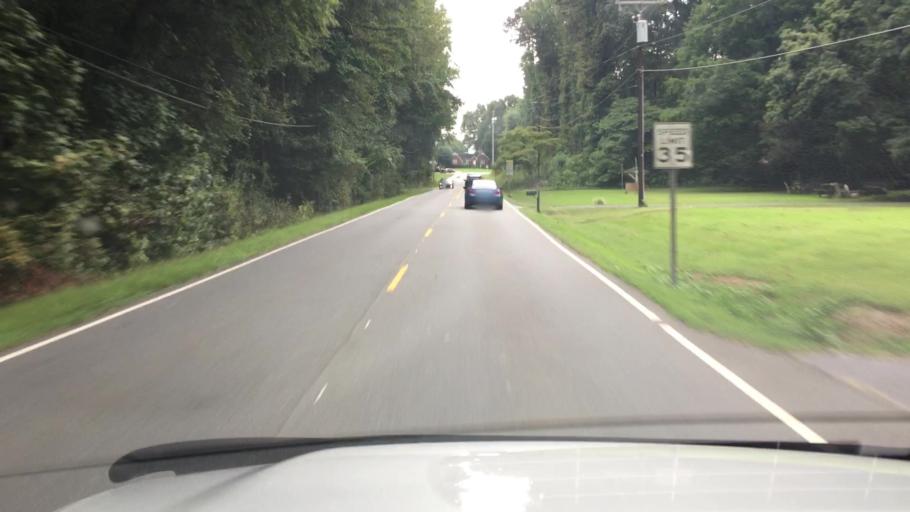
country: US
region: North Carolina
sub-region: Mecklenburg County
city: Huntersville
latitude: 35.3551
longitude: -80.8911
